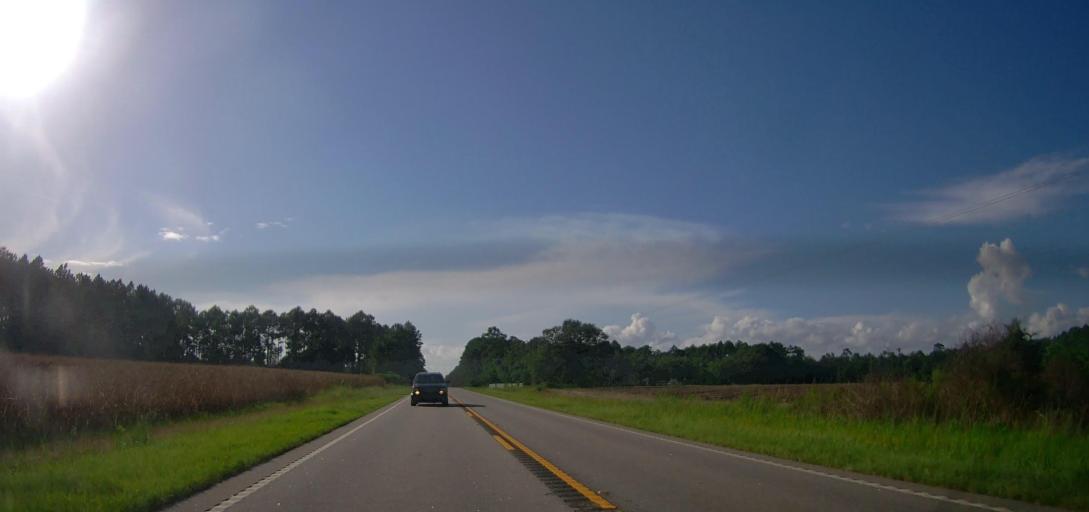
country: US
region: Georgia
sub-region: Coffee County
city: Nicholls
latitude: 31.4385
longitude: -82.7132
